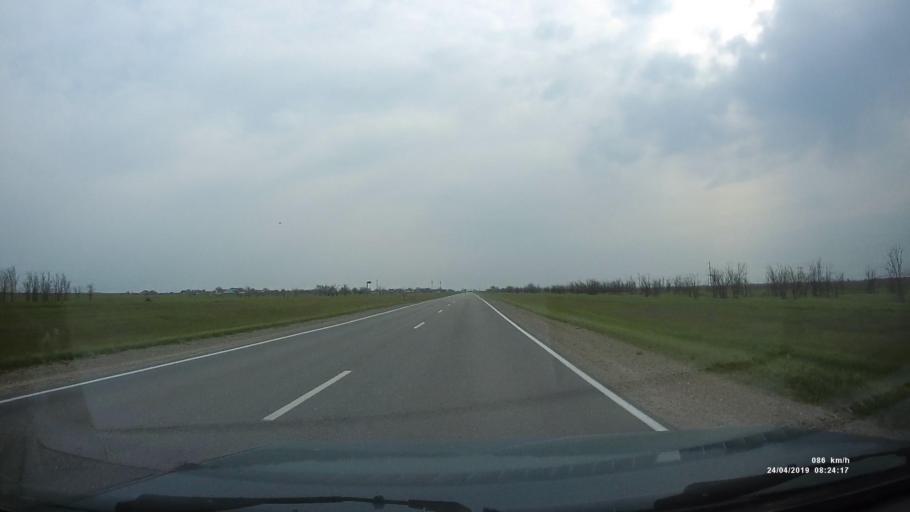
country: RU
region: Kalmykiya
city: Priyutnoye
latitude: 46.1201
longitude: 43.7519
